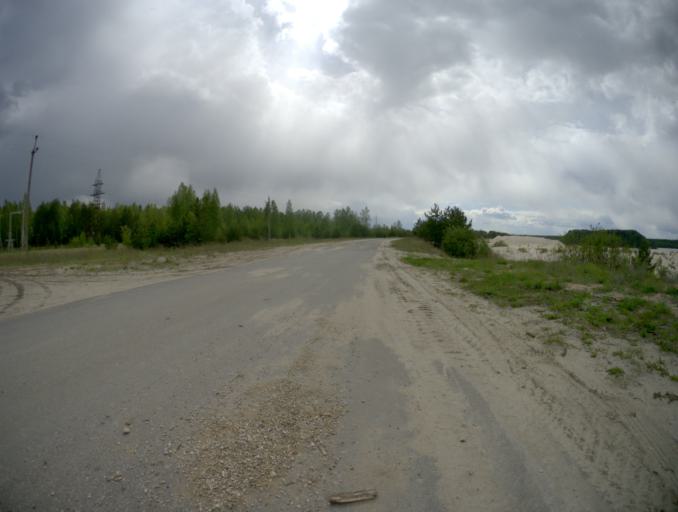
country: RU
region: Vladimir
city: Velikodvorskiy
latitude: 55.2316
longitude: 40.6531
